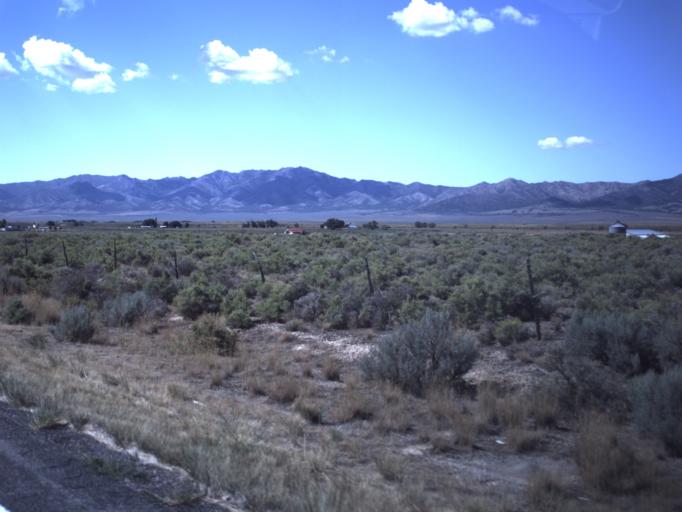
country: US
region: Utah
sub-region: Tooele County
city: Tooele
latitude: 40.1176
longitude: -112.4308
